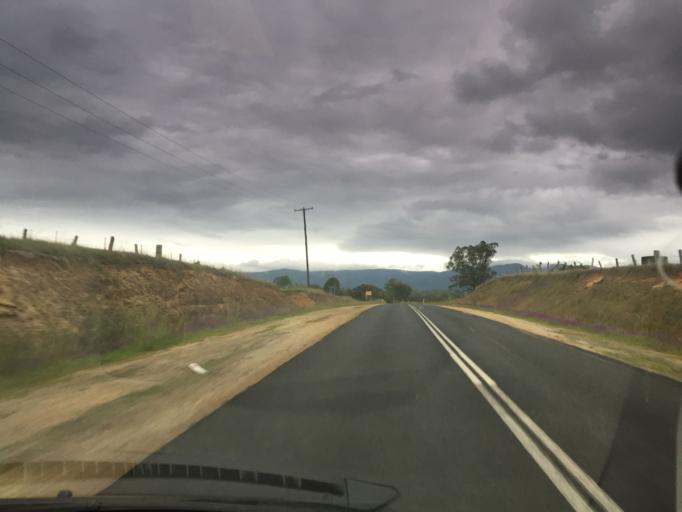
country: AU
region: New South Wales
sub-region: Bega Valley
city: Bega
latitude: -36.6456
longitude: 149.5859
